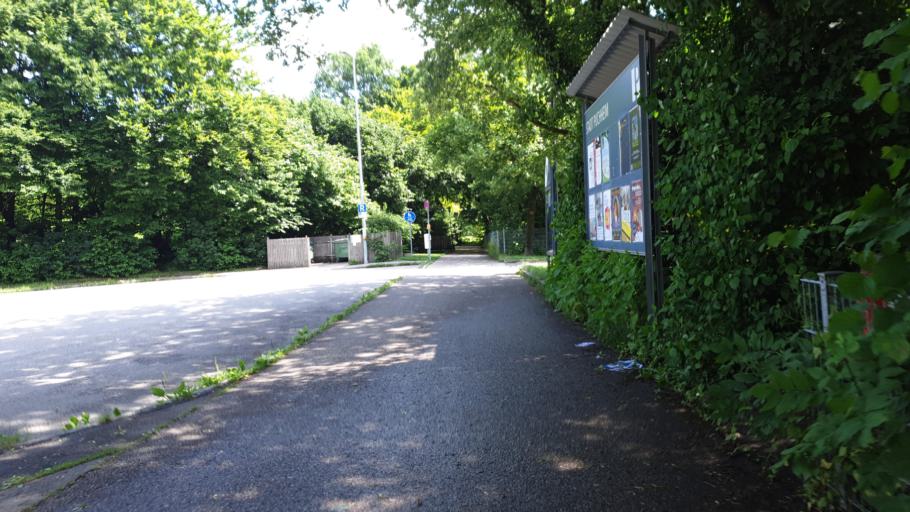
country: DE
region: Bavaria
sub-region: Upper Bavaria
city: Puchheim
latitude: 48.1648
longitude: 11.3489
